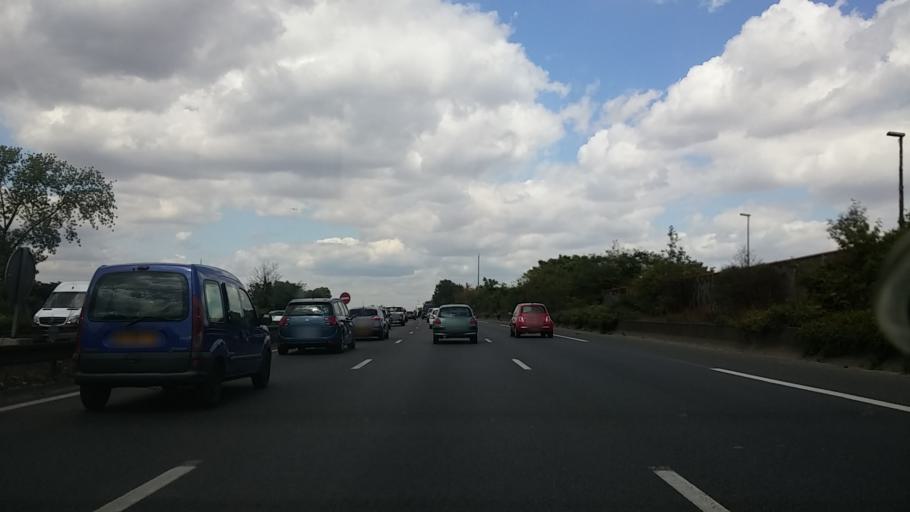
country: FR
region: Ile-de-France
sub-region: Departement de Seine-Saint-Denis
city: Aulnay-sous-Bois
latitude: 48.9261
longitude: 2.4815
